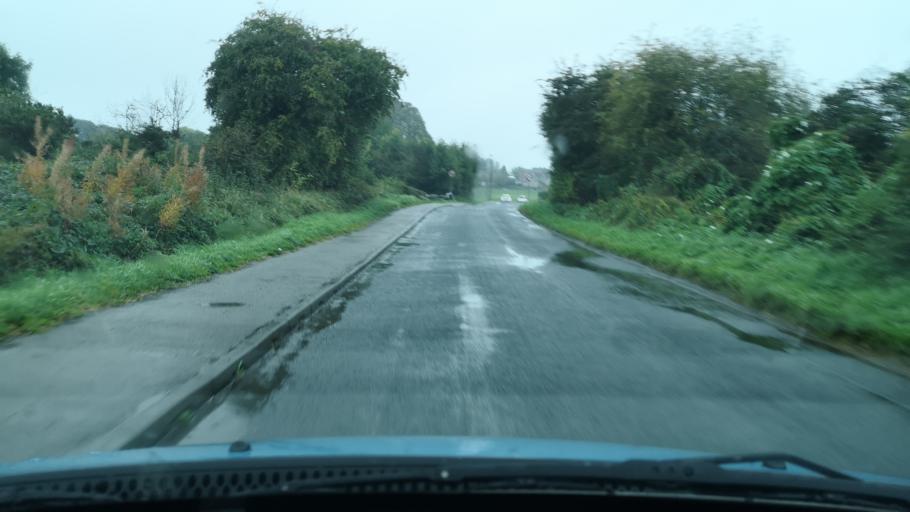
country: GB
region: England
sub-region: City and Borough of Wakefield
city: Sharlston
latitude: 53.6673
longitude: -1.4062
